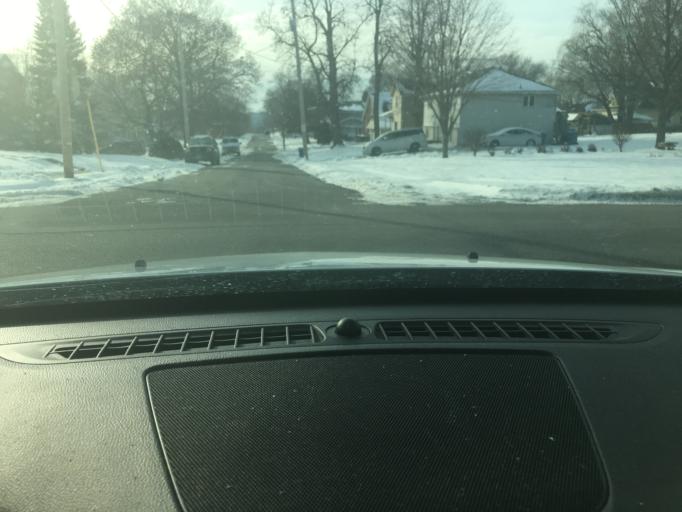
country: US
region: Illinois
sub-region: LaSalle County
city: Peru
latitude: 41.3305
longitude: -89.1209
